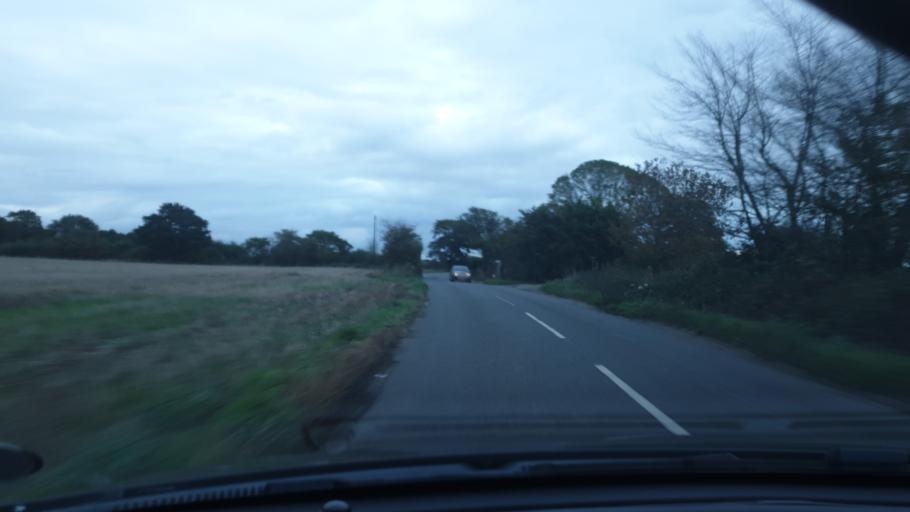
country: GB
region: England
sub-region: Essex
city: Clacton-on-Sea
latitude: 51.8100
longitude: 1.1799
